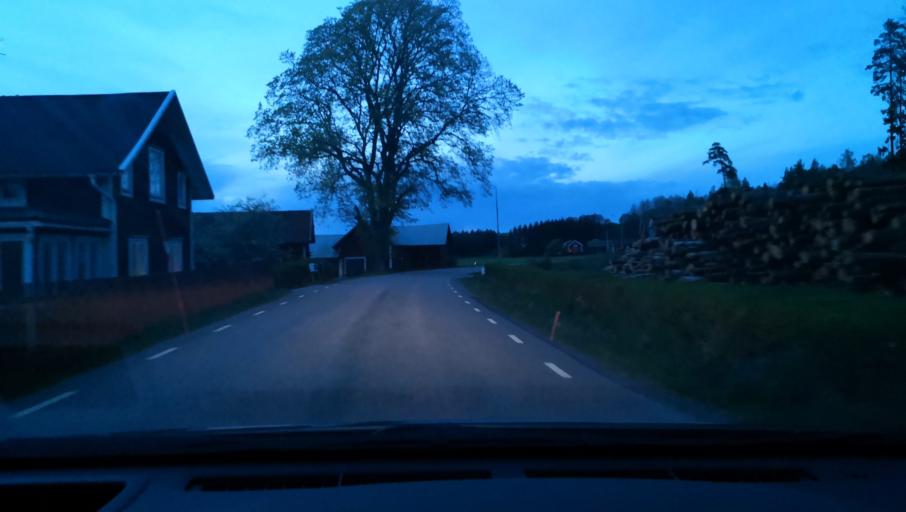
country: SE
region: OErebro
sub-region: Askersunds Kommun
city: Asbro
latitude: 59.0725
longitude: 15.0045
